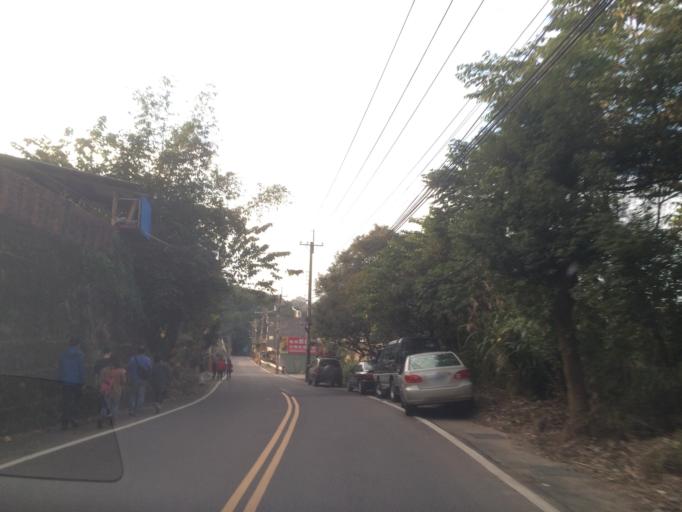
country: TW
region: Taiwan
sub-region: Hsinchu
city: Hsinchu
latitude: 24.6934
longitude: 121.1002
